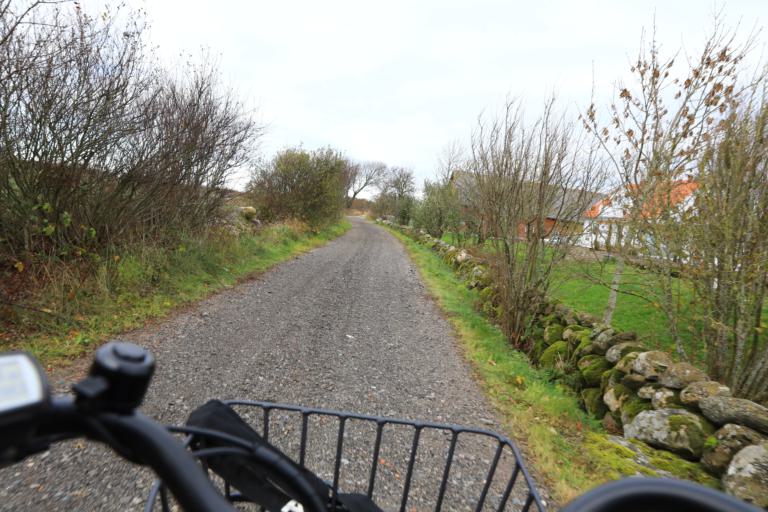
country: SE
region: Halland
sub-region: Varbergs Kommun
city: Traslovslage
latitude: 57.0540
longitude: 12.3374
